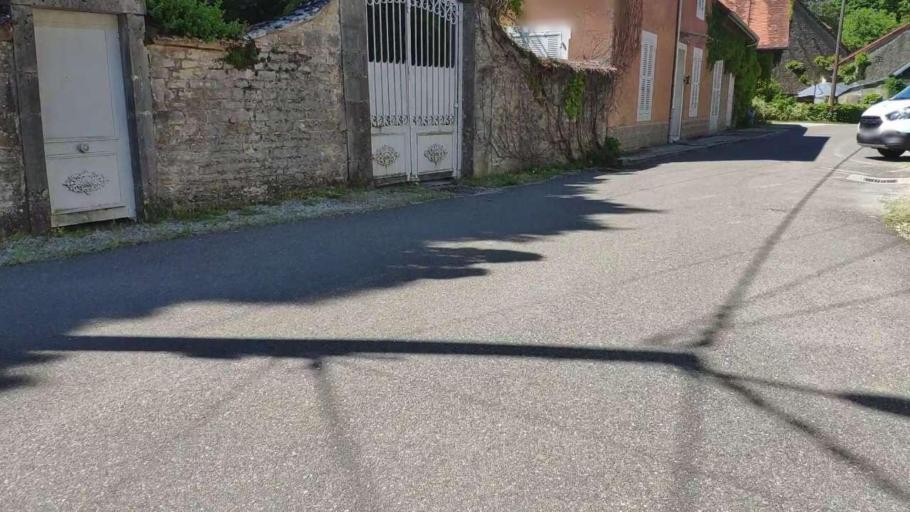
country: FR
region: Franche-Comte
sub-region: Departement du Jura
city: Perrigny
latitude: 46.7528
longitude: 5.6115
